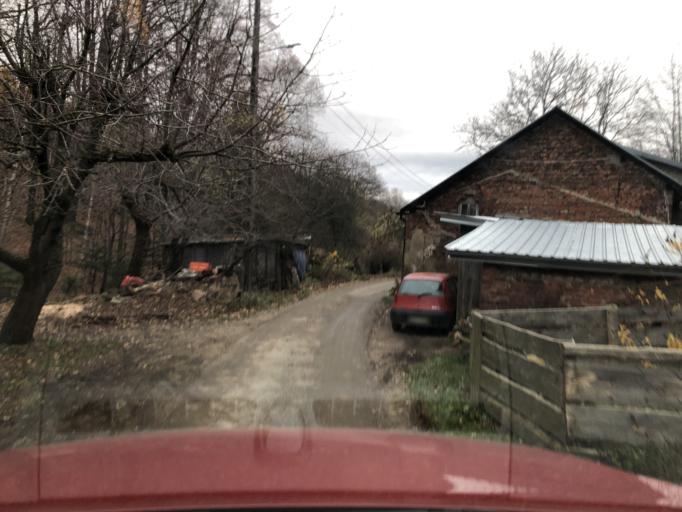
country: PL
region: Lower Silesian Voivodeship
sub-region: Powiat walbrzyski
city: Stare Bogaczowice
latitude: 50.8038
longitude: 16.1866
